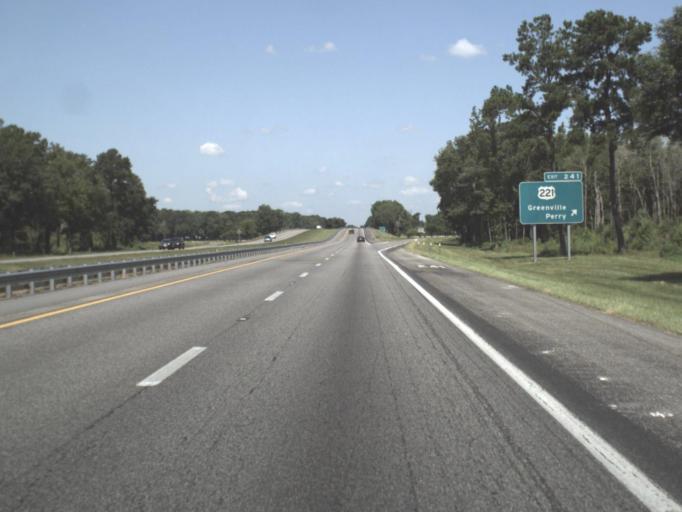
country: US
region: Florida
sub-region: Madison County
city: Madison
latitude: 30.4328
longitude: -83.6203
